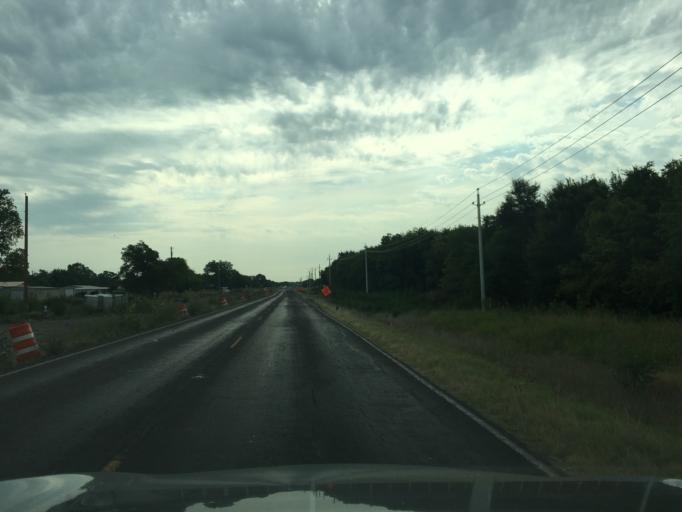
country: US
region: Texas
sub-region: Collin County
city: Lucas
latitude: 33.0550
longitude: -96.5893
